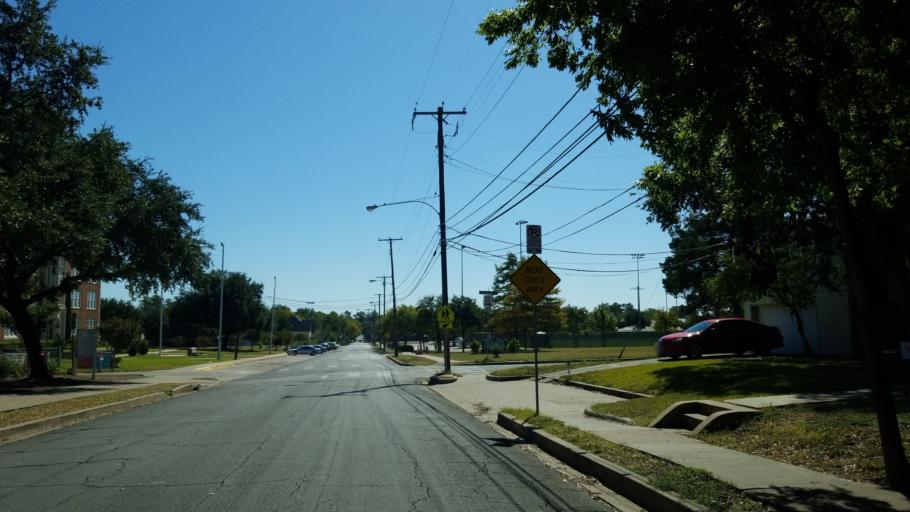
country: US
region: Texas
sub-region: Dallas County
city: Highland Park
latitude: 32.8058
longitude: -96.7518
